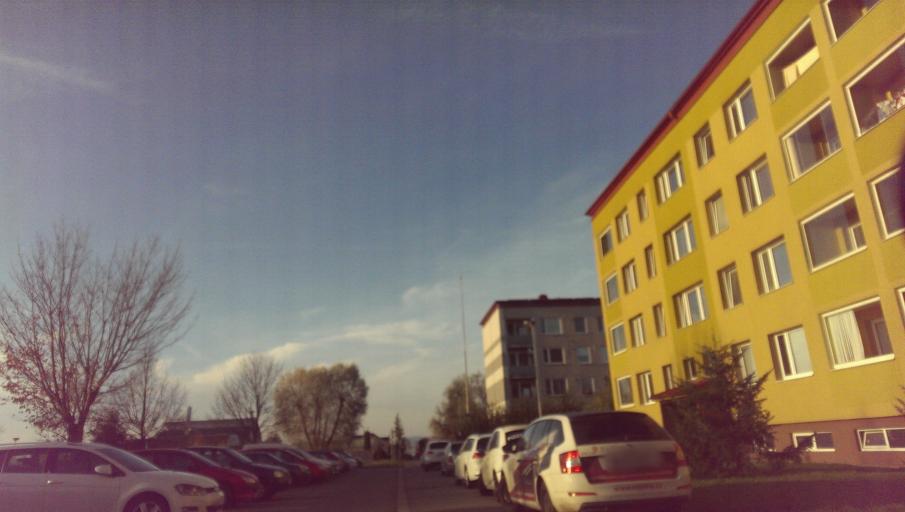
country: CZ
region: Zlin
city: Kunovice
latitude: 49.0593
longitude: 17.4796
